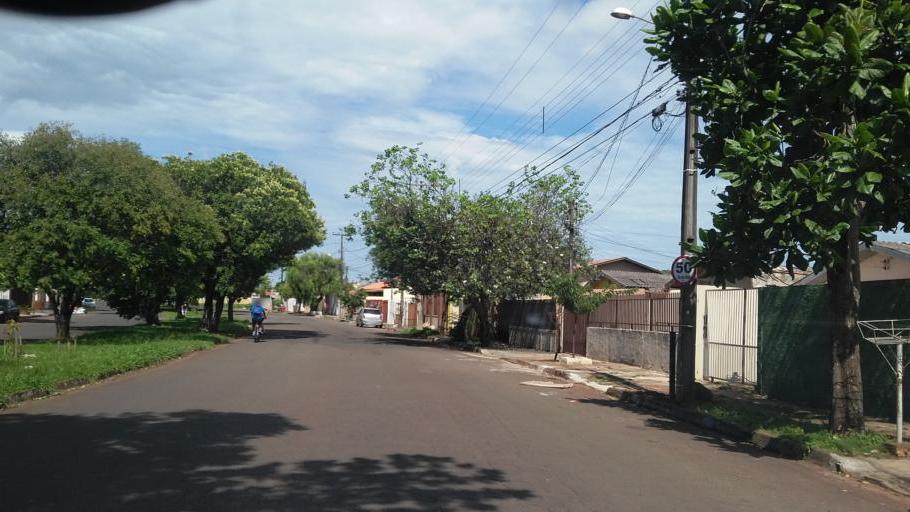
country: BR
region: Parana
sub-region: Londrina
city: Londrina
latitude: -23.2848
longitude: -51.2026
